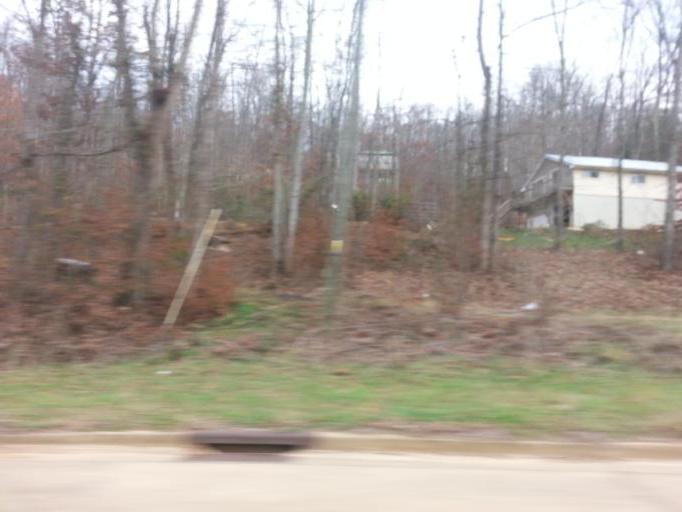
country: US
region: Tennessee
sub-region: Hamilton County
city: Sale Creek
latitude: 35.4032
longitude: -85.1027
